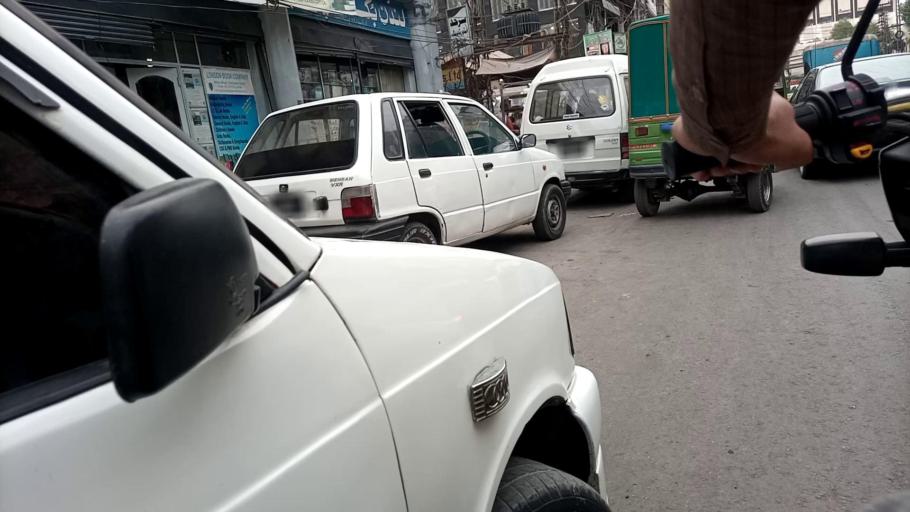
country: PK
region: Khyber Pakhtunkhwa
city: Peshawar
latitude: 33.9979
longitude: 71.5370
